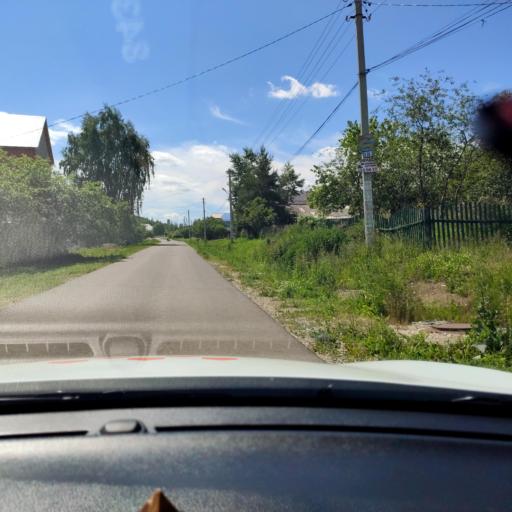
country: RU
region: Tatarstan
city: Sviyazhsk
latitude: 55.7706
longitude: 48.7666
